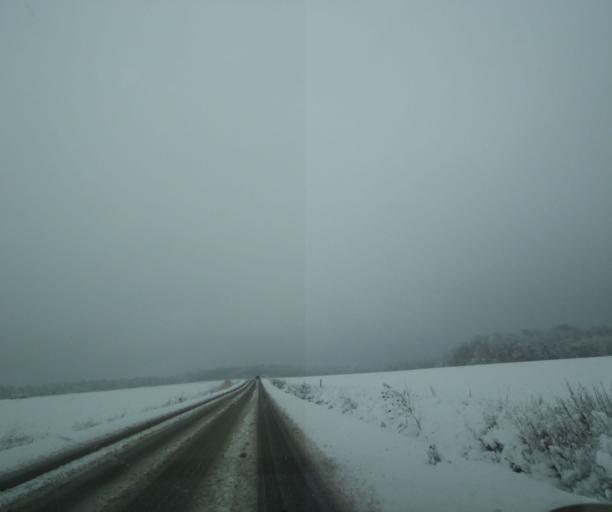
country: FR
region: Champagne-Ardenne
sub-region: Departement de la Haute-Marne
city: Saint-Dizier
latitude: 48.5943
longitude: 4.9048
